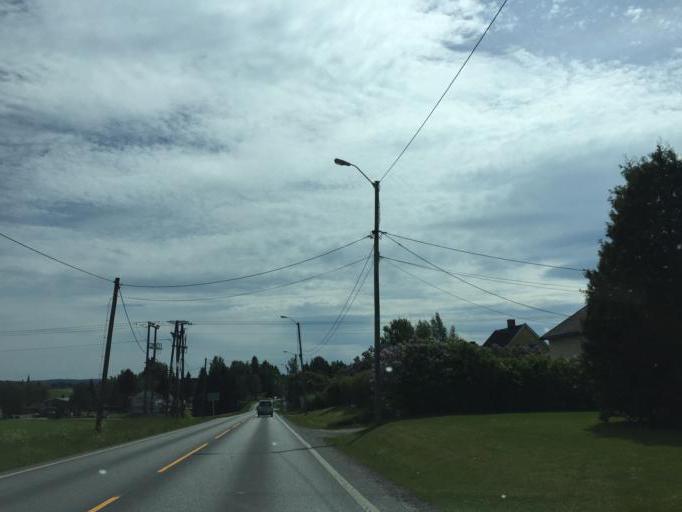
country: NO
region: Akershus
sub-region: Nes
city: Arnes
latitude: 60.1282
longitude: 11.4460
